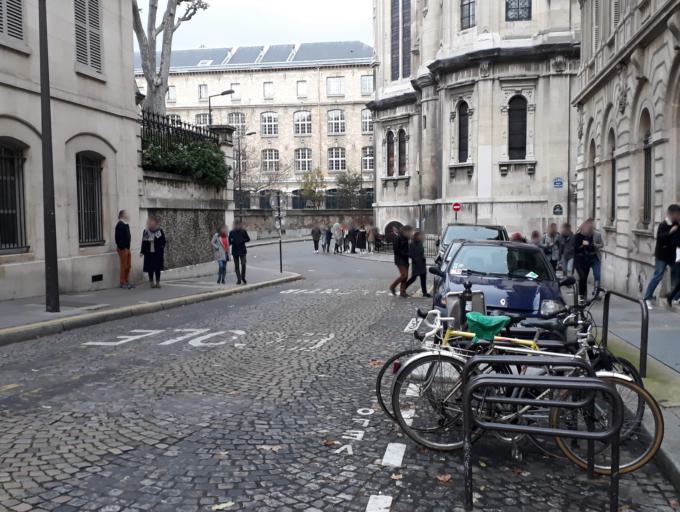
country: FR
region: Ile-de-France
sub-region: Paris
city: Saint-Ouen
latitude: 48.8775
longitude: 2.3305
